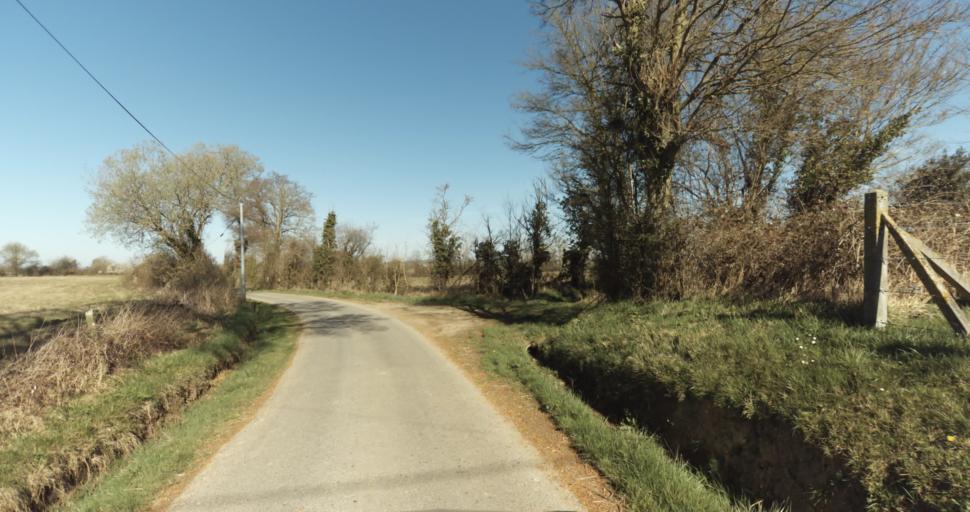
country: FR
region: Lower Normandy
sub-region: Departement de l'Orne
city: Trun
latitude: 48.9175
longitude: 0.0382
